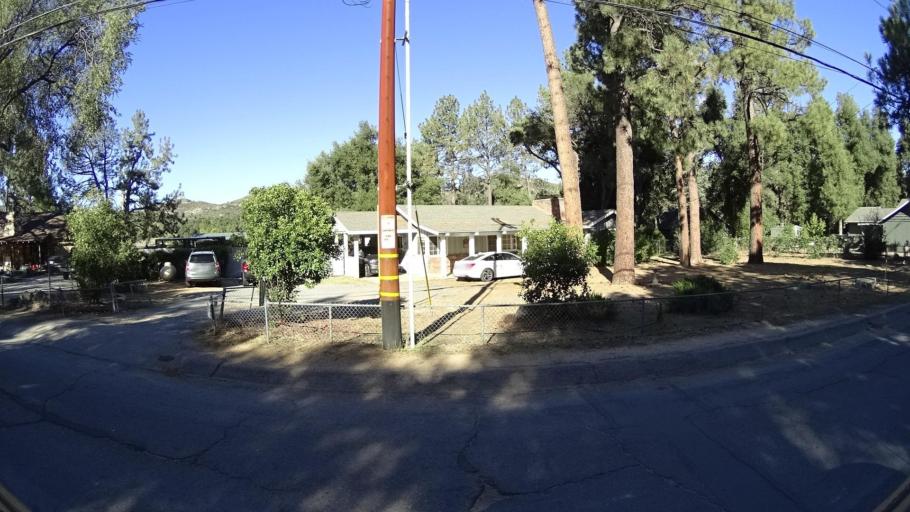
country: US
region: California
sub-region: San Diego County
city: Pine Valley
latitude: 32.8246
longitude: -116.5261
